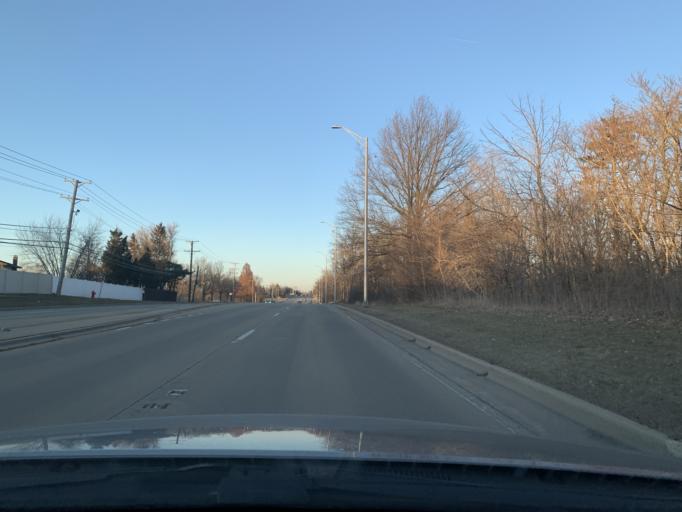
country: US
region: Illinois
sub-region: Cook County
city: Schaumburg
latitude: 42.0225
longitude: -88.0603
